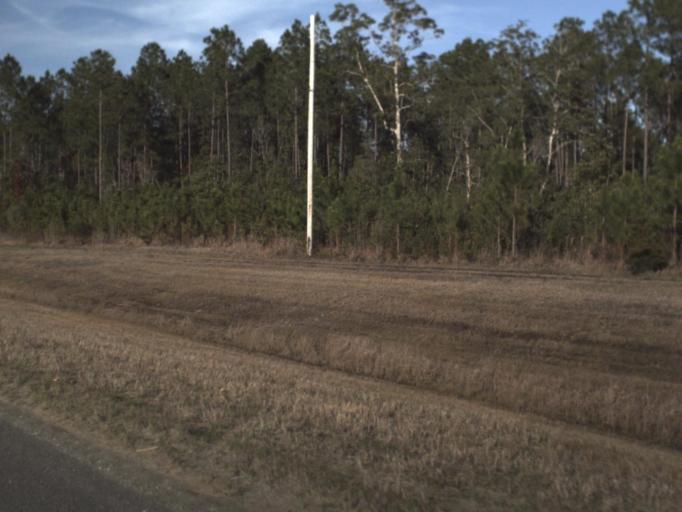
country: US
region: Florida
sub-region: Bay County
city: Laguna Beach
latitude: 30.3531
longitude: -85.8588
